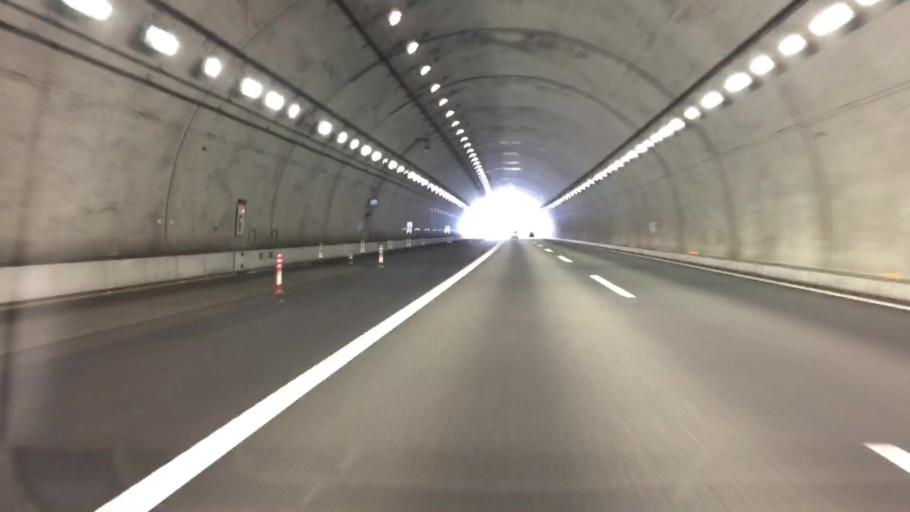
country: JP
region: Shizuoka
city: Mishima
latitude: 35.1838
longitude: 138.8877
